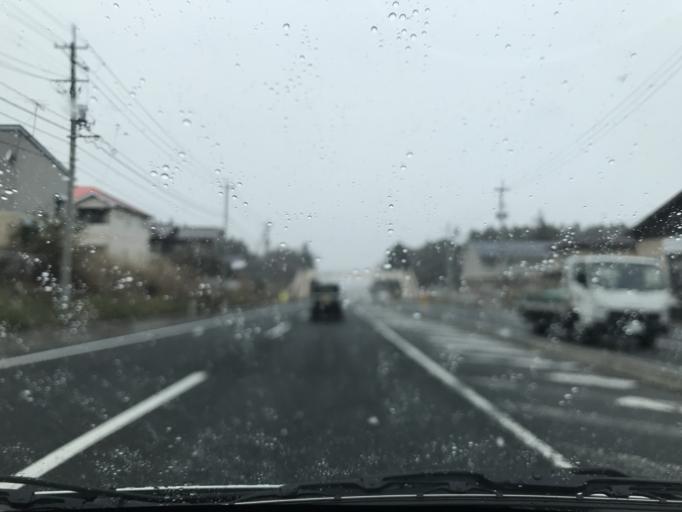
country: JP
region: Iwate
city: Kitakami
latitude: 39.2641
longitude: 141.0992
